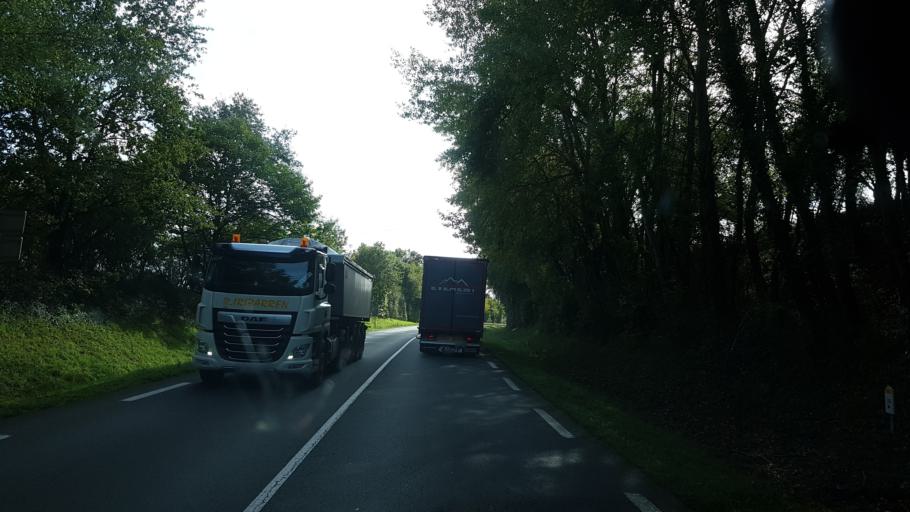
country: FR
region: Poitou-Charentes
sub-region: Departement de la Charente
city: Confolens
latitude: 46.0305
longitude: 0.6589
